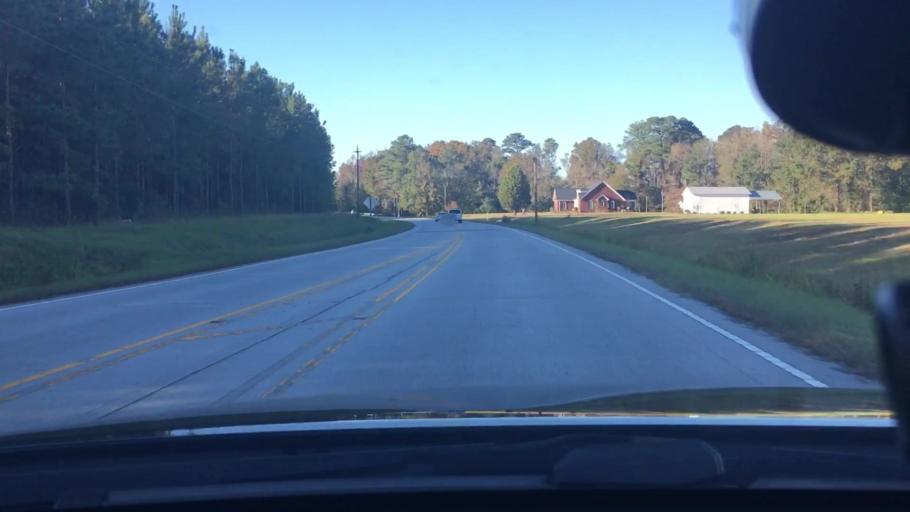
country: US
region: North Carolina
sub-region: Craven County
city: Vanceboro
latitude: 35.3340
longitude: -77.1723
